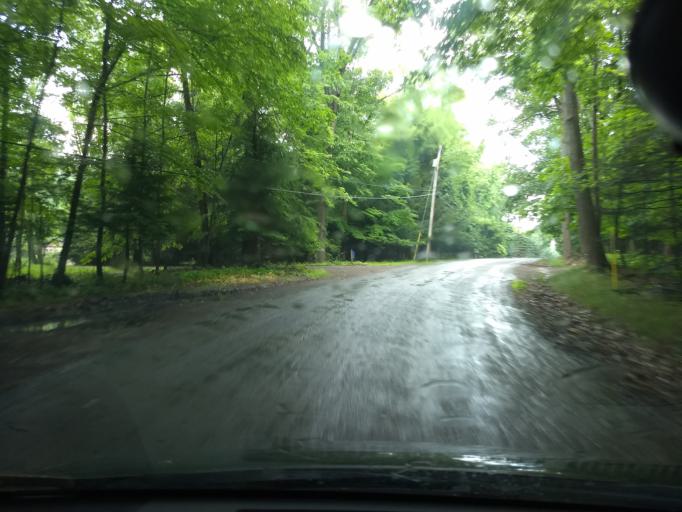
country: US
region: Pennsylvania
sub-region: Armstrong County
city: Orchard Hills
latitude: 40.5556
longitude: -79.5083
